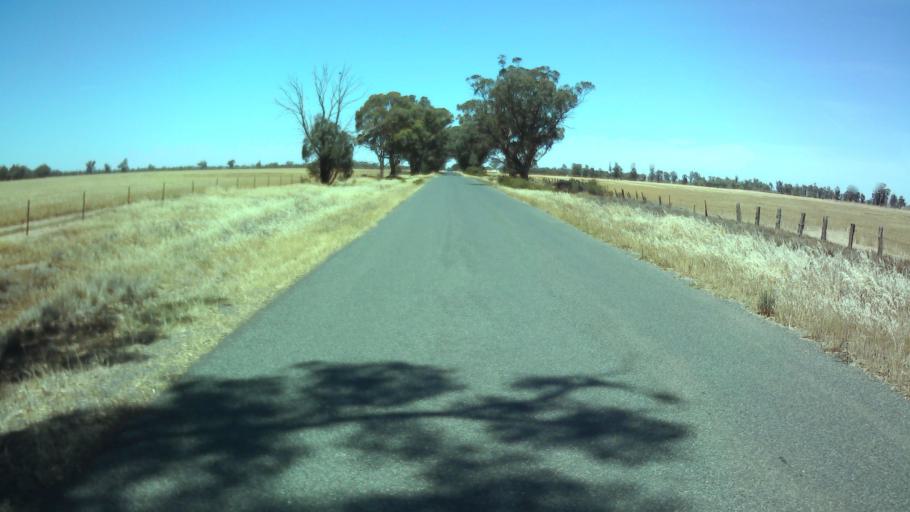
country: AU
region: New South Wales
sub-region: Weddin
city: Grenfell
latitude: -34.0205
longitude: 147.7927
